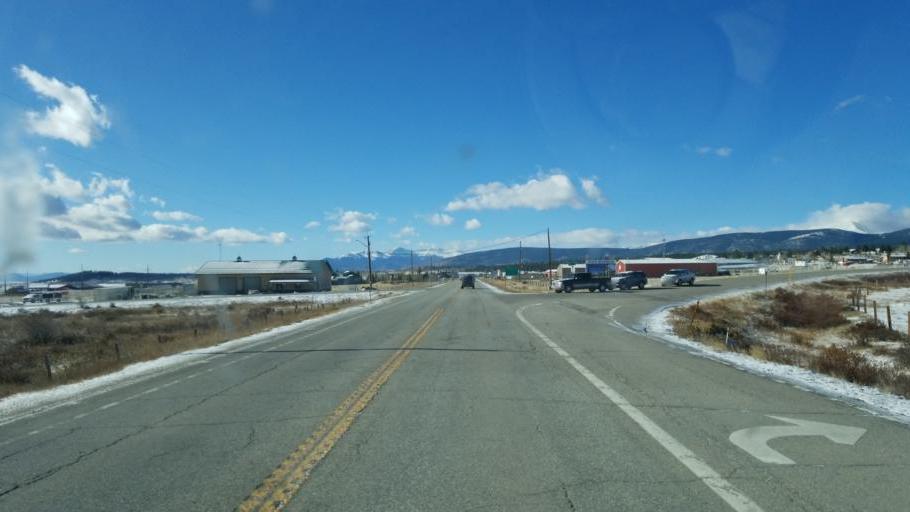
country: US
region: Colorado
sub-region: Park County
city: Fairplay
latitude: 39.2295
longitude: -105.9883
